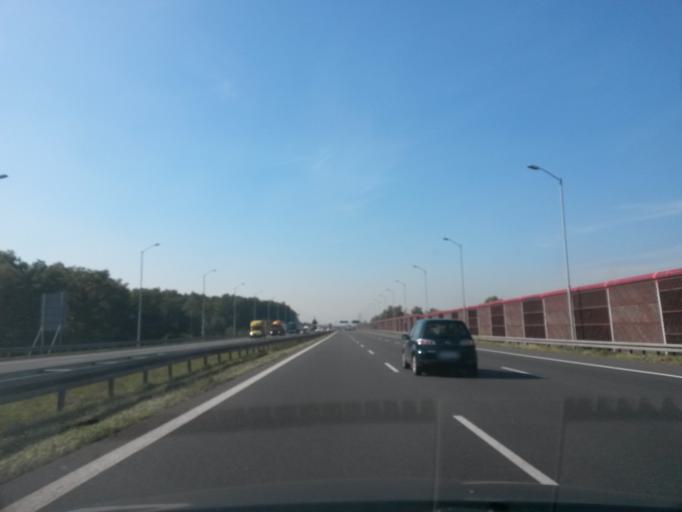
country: PL
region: Silesian Voivodeship
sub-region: Ruda Slaska
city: Ruda Slaska
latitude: 50.2540
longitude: 18.8691
